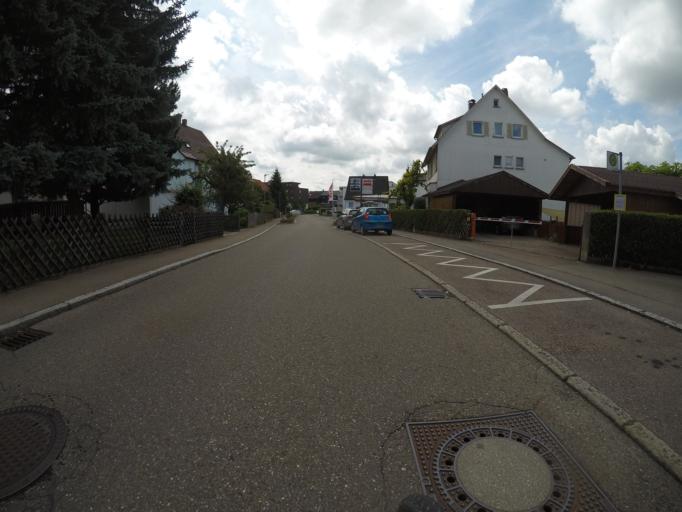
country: DE
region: Baden-Wuerttemberg
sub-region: Regierungsbezirk Stuttgart
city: Salach
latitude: 48.6939
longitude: 9.7373
